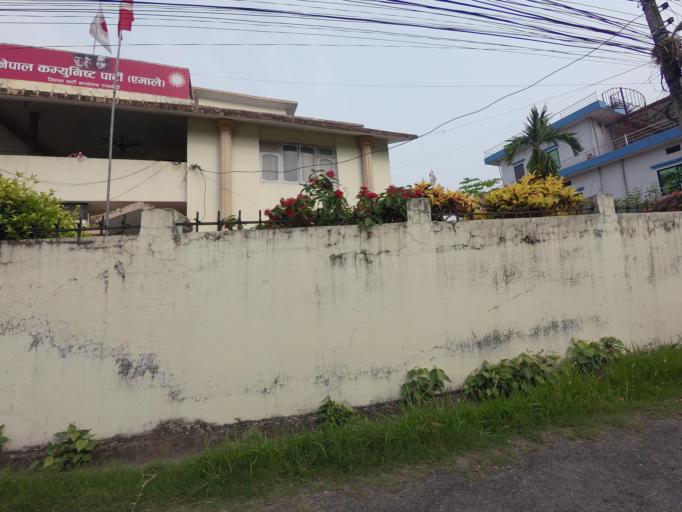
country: NP
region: Western Region
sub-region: Lumbini Zone
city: Bhairahawa
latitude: 27.5199
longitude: 83.4517
